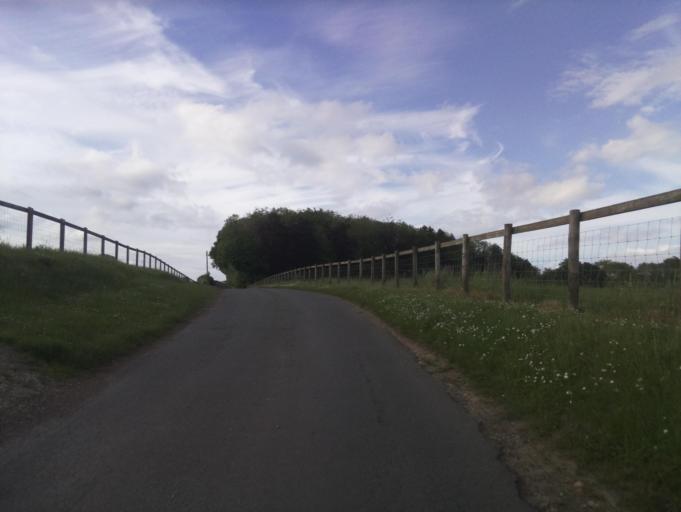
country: GB
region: England
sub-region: Gloucestershire
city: Westfield
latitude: 51.8834
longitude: -1.8883
